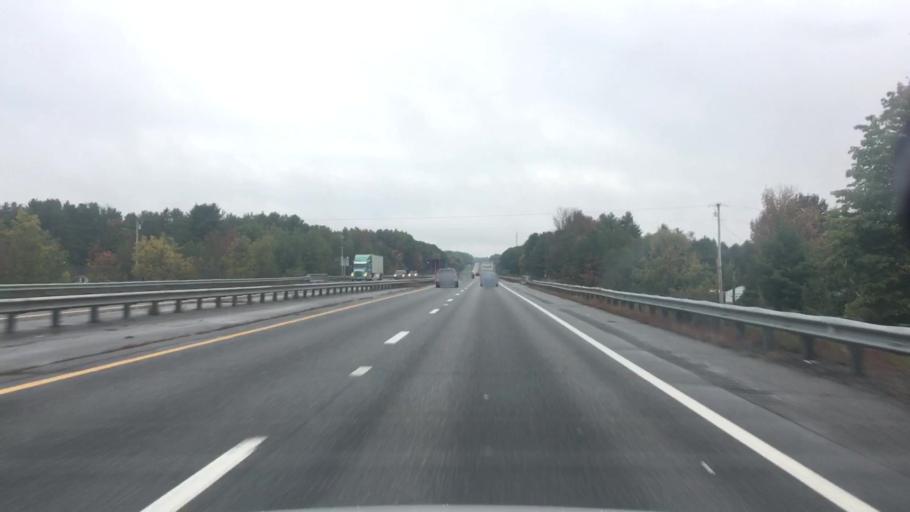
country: US
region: Maine
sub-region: Kennebec County
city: Gardiner
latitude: 44.2440
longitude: -69.8075
